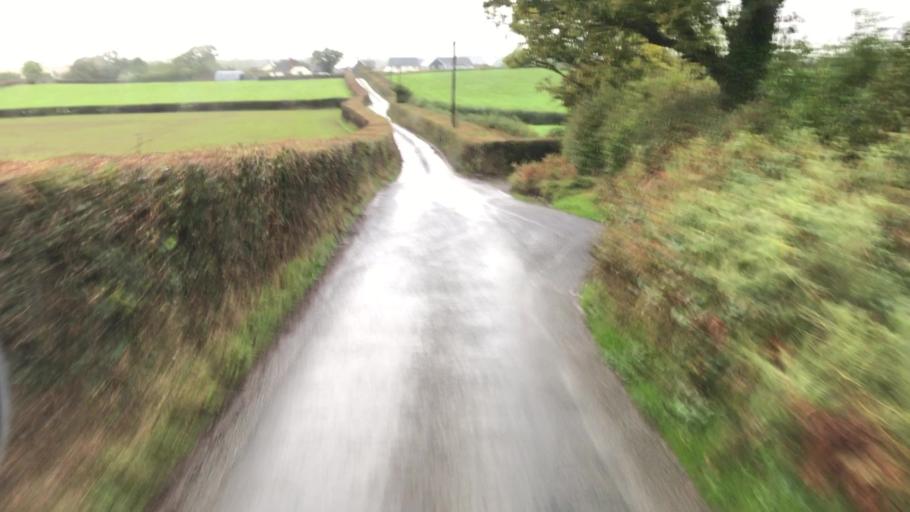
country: GB
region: England
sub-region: Devon
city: Crediton
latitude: 50.7205
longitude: -3.7338
